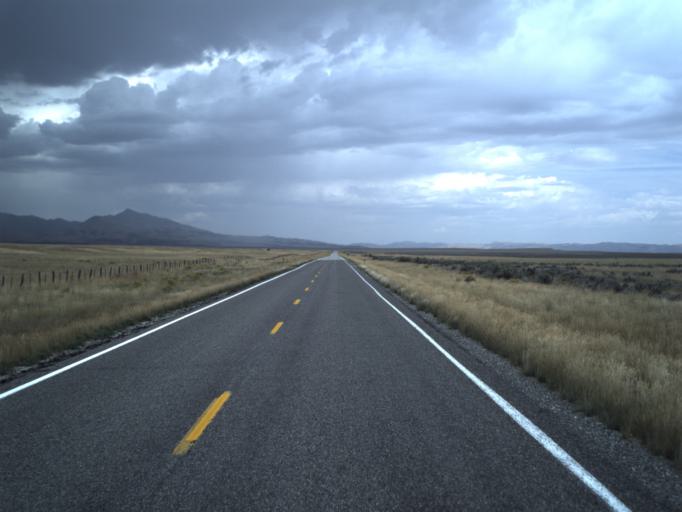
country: US
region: Idaho
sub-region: Oneida County
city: Malad City
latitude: 41.9152
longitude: -113.0983
